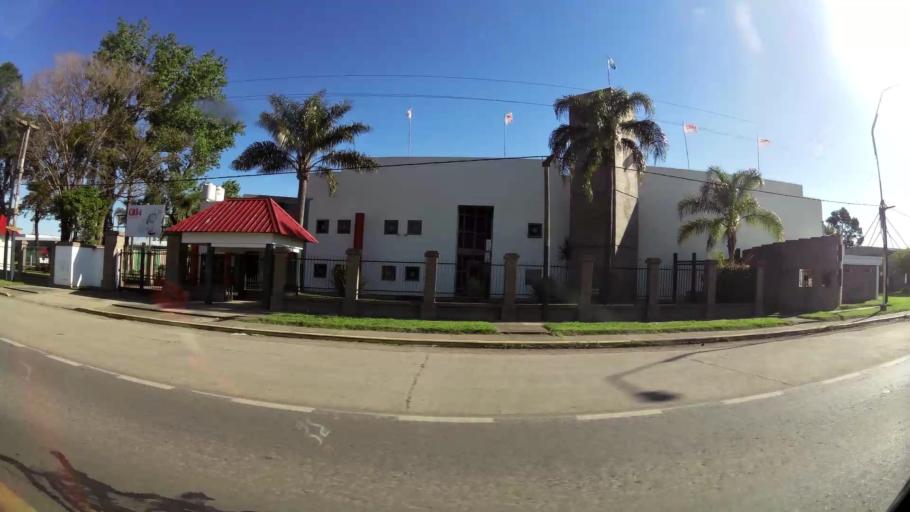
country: AR
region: Cordoba
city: San Francisco
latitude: -31.4241
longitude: -62.0531
